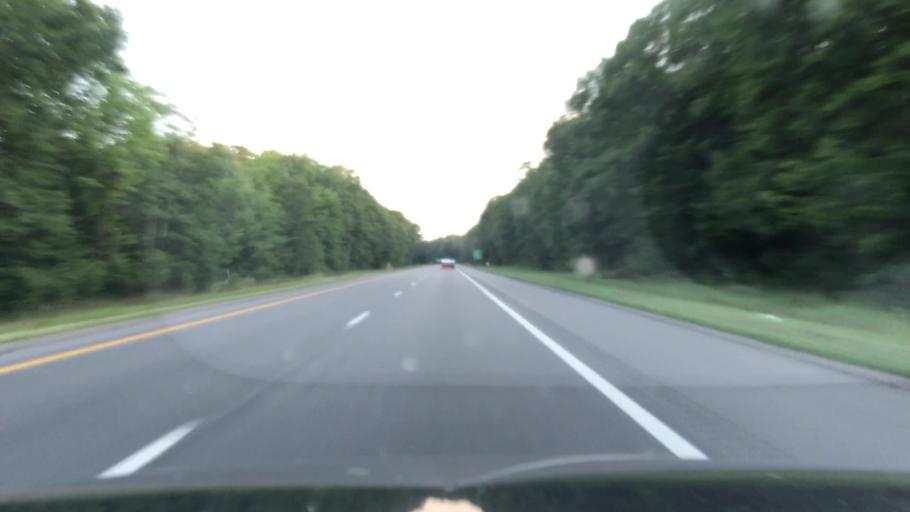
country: US
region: Michigan
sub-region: Montcalm County
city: Howard City
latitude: 43.4483
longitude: -85.4883
